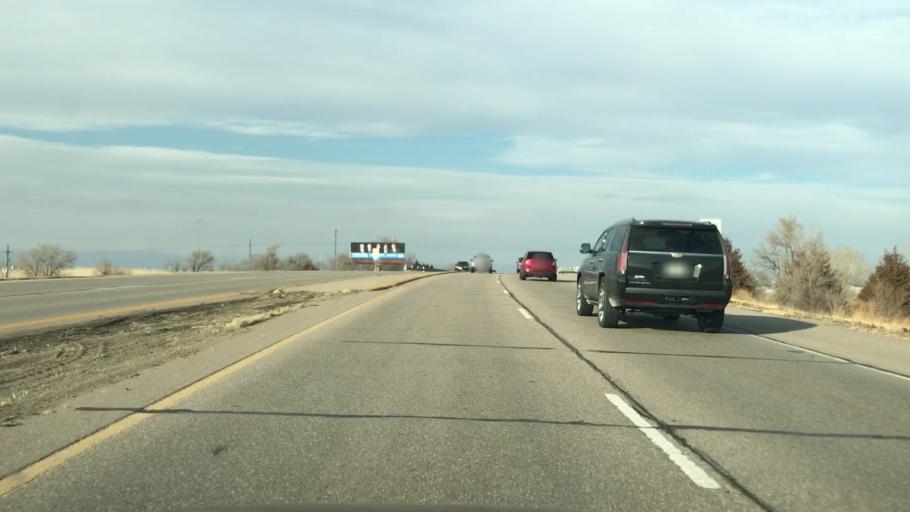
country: US
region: Nebraska
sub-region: Hall County
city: Grand Island
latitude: 40.9067
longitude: -98.3831
